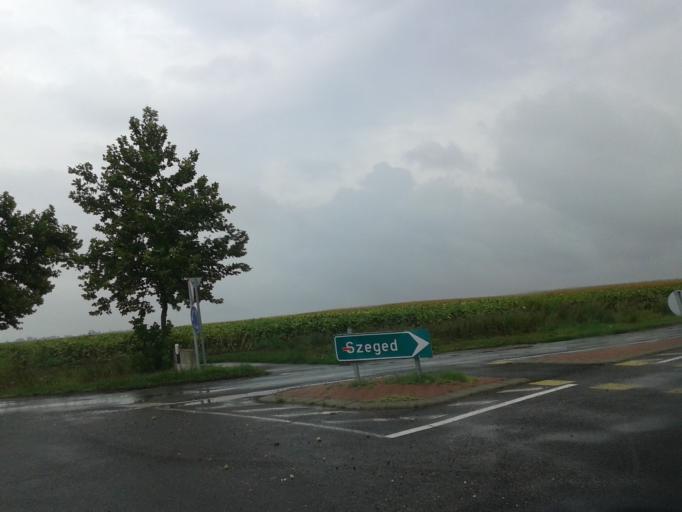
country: HU
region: Csongrad
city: Szeged
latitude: 46.2520
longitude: 20.0820
